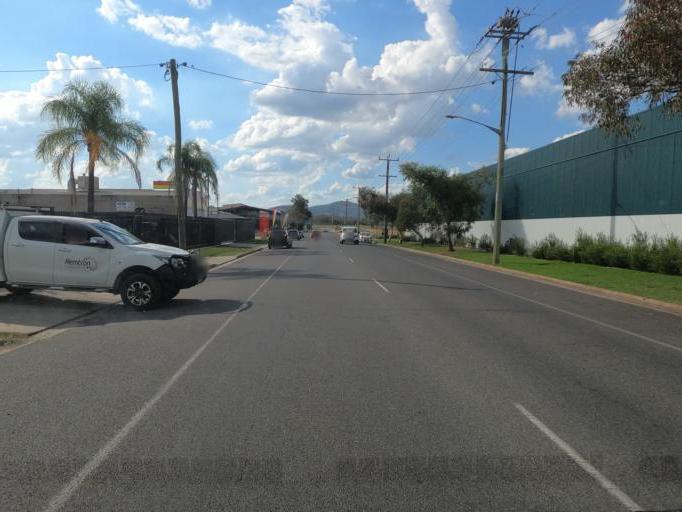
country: AU
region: New South Wales
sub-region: Albury Municipality
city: East Albury
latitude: -36.0736
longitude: 146.9479
